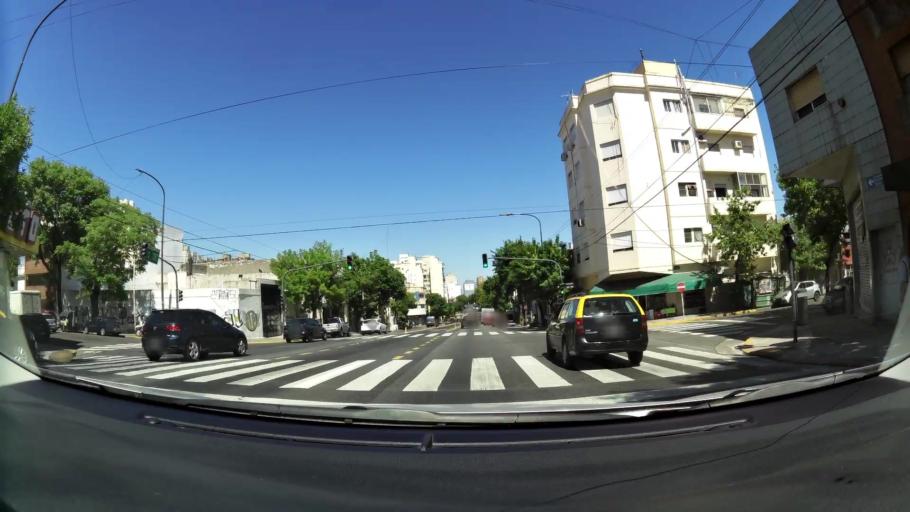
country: AR
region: Buenos Aires F.D.
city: Buenos Aires
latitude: -34.6288
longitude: -58.4024
